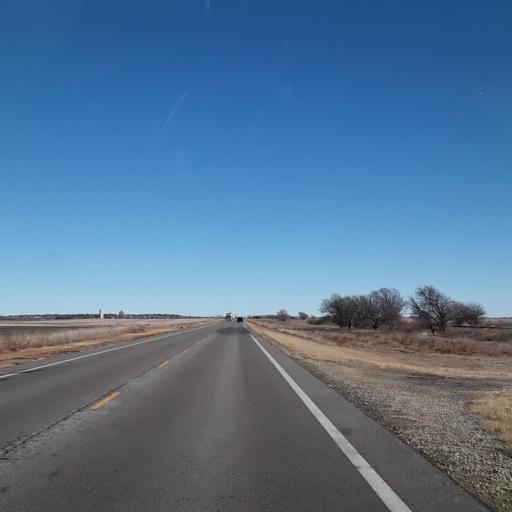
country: US
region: Kansas
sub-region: Pawnee County
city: Larned
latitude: 38.1452
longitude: -99.1428
